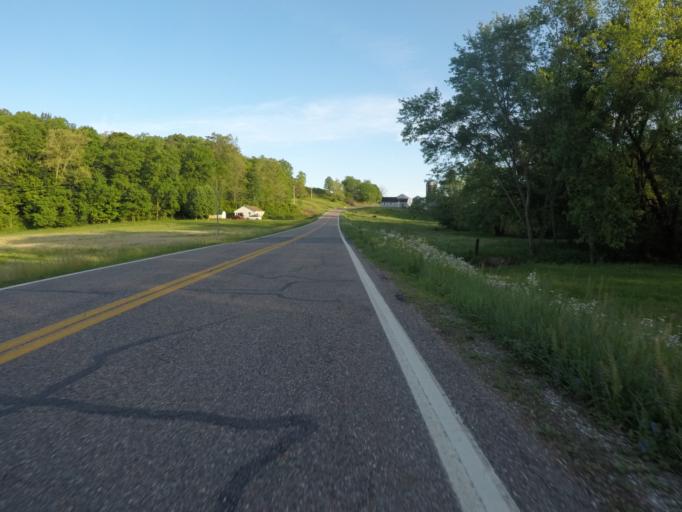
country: US
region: West Virginia
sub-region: Cabell County
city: Huntington
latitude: 38.5346
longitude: -82.4602
